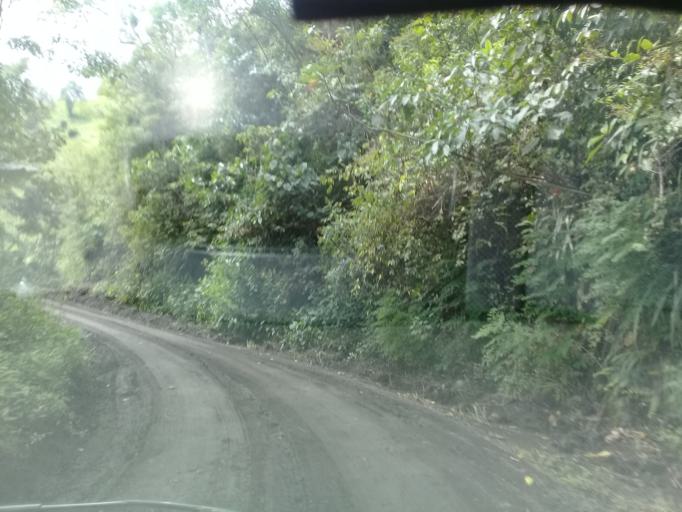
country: CO
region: Cundinamarca
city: Quipile
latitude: 4.7263
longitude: -74.5374
